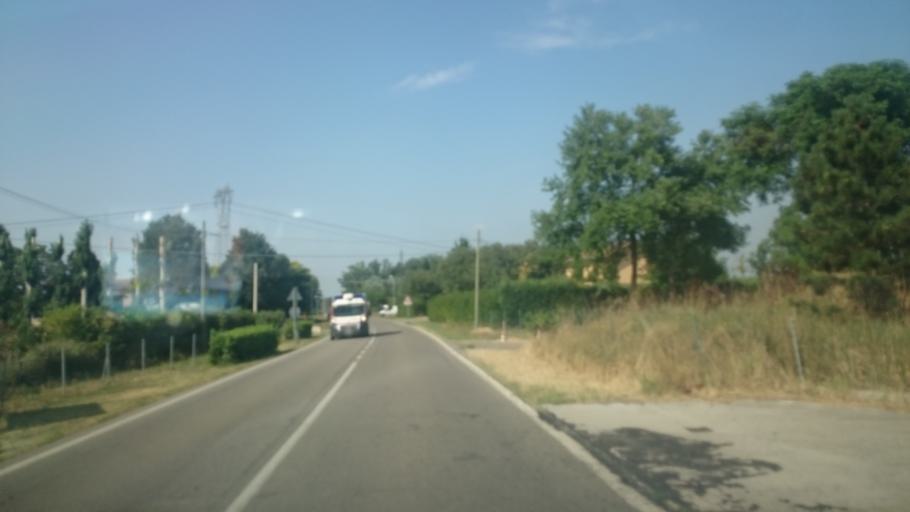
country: IT
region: Emilia-Romagna
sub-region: Provincia di Reggio Emilia
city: Arceto
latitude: 44.6382
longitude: 10.7353
